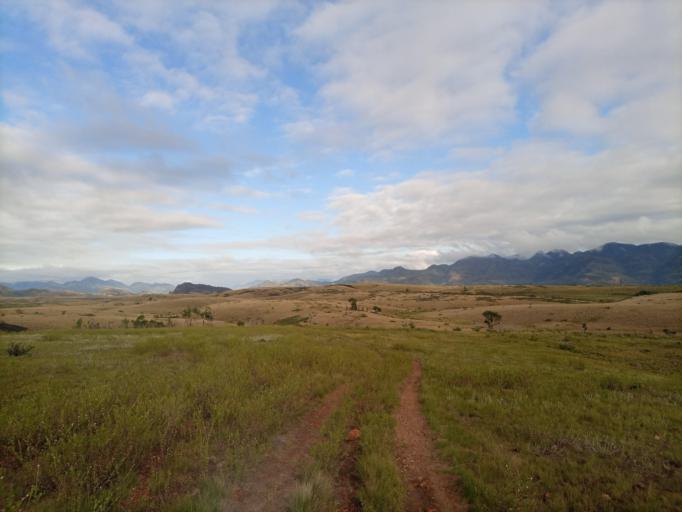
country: MG
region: Anosy
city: Fort Dauphin
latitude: -24.3089
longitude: 47.2468
